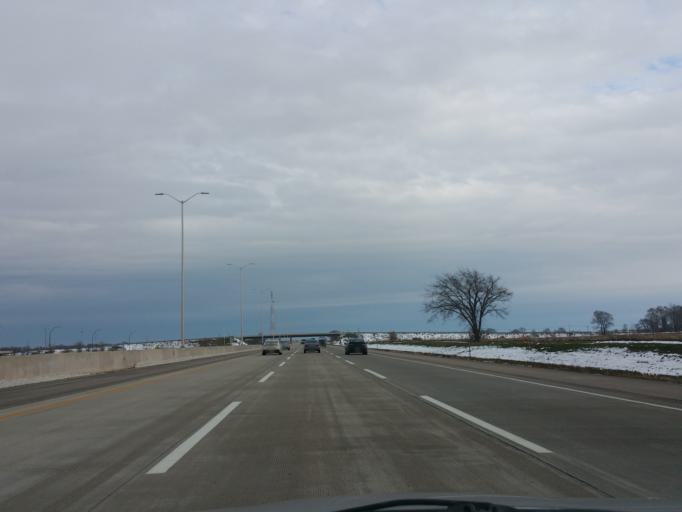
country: US
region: Illinois
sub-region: Boone County
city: Belvidere
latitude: 42.2332
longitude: -88.8678
